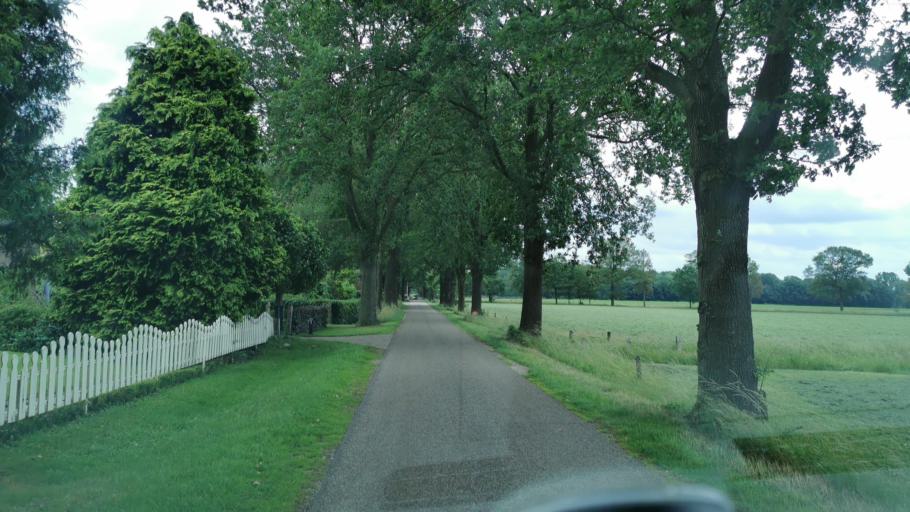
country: DE
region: North Rhine-Westphalia
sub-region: Regierungsbezirk Munster
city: Gronau
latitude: 52.2304
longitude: 7.0212
